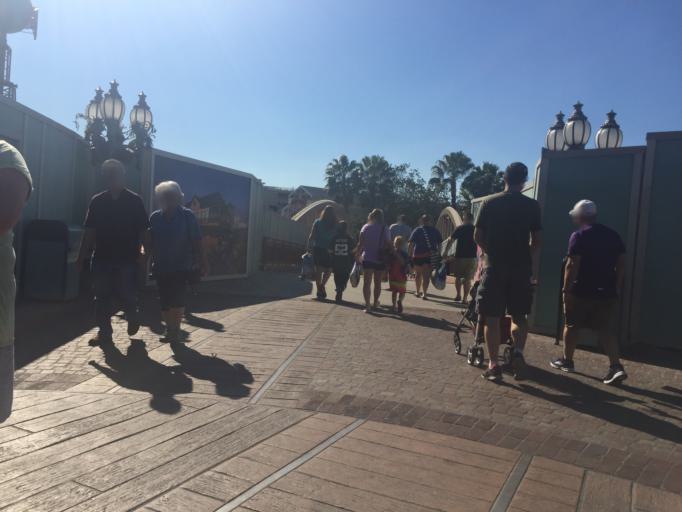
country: US
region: Florida
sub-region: Osceola County
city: Celebration
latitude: 28.3706
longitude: -81.5187
